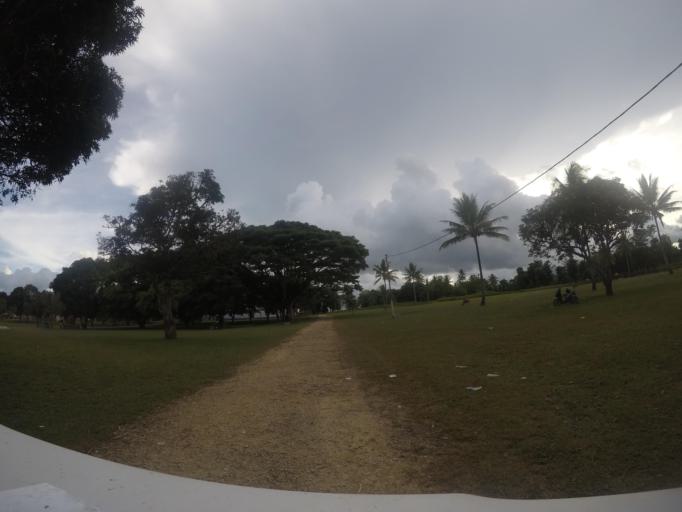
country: TL
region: Lautem
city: Lospalos
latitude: -8.5068
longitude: 126.9865
